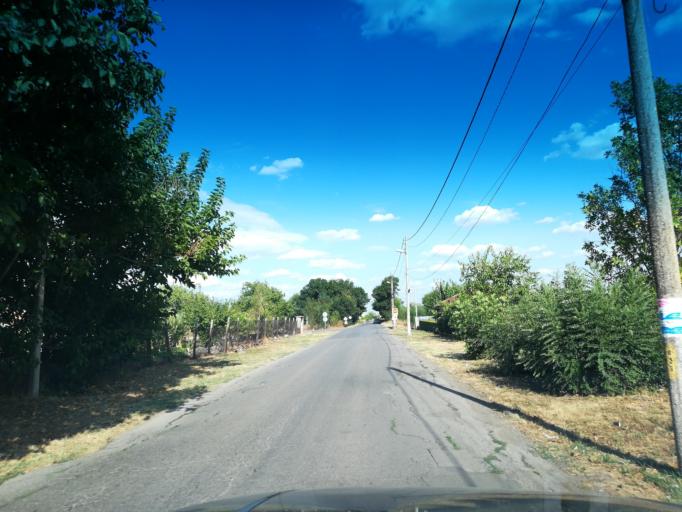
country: BG
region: Khaskovo
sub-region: Obshtina Mineralni Bani
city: Mineralni Bani
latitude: 42.0221
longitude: 25.4292
